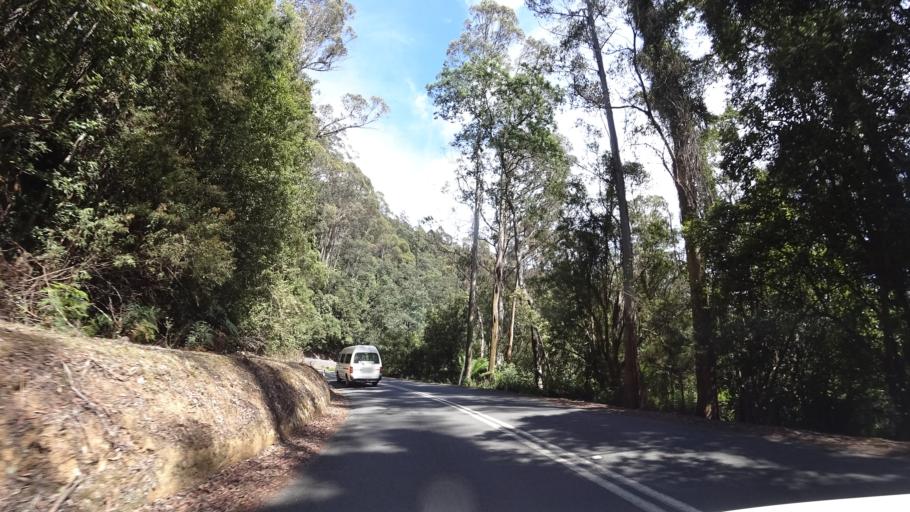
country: AU
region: Tasmania
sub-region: Break O'Day
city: St Helens
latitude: -41.1640
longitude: 147.8978
